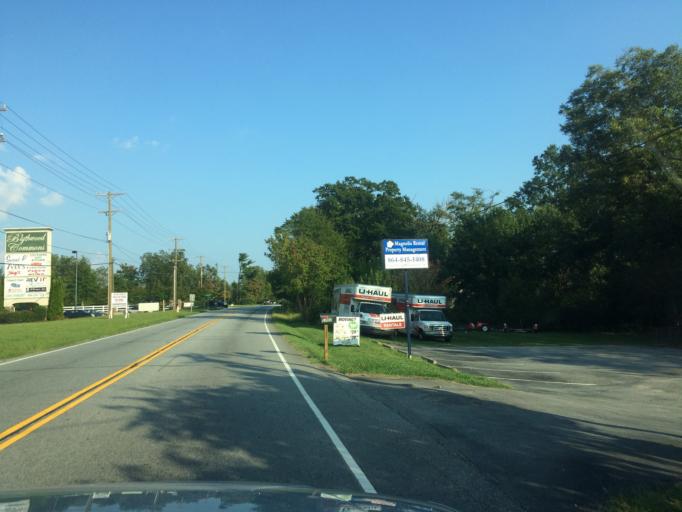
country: US
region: South Carolina
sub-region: Anderson County
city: Piedmont
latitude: 34.7082
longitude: -82.4932
